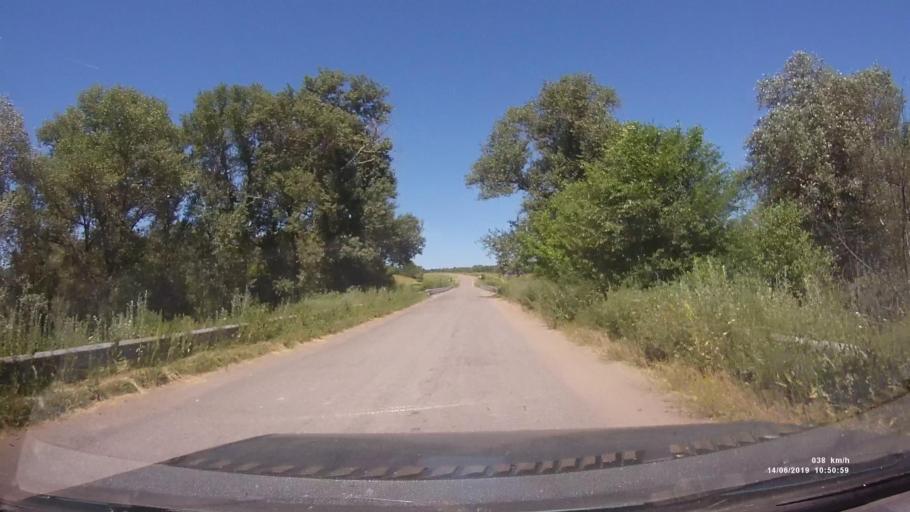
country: RU
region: Rostov
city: Kazanskaya
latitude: 49.8681
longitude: 41.3953
